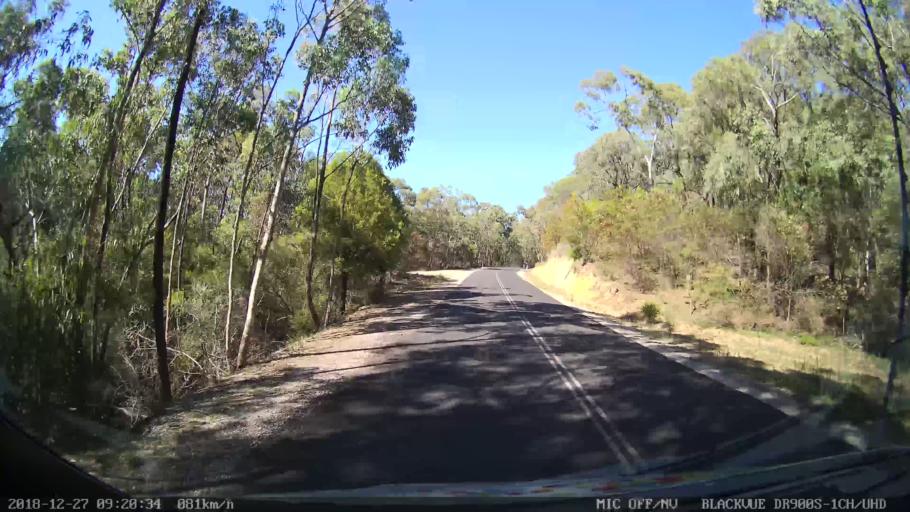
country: AU
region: New South Wales
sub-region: Lithgow
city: Portland
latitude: -33.1207
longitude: 150.0214
